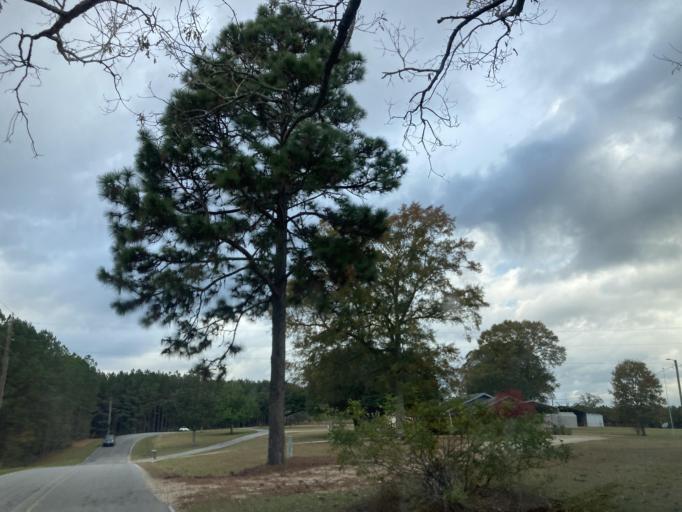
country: US
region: Mississippi
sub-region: Marion County
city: Columbia
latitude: 31.1900
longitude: -89.6689
